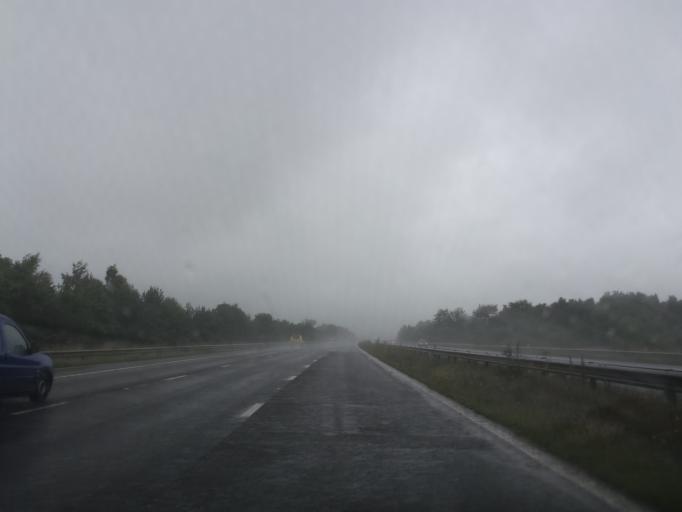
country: GB
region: England
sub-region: Leicestershire
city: Shepshed
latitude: 52.7454
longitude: -1.2769
